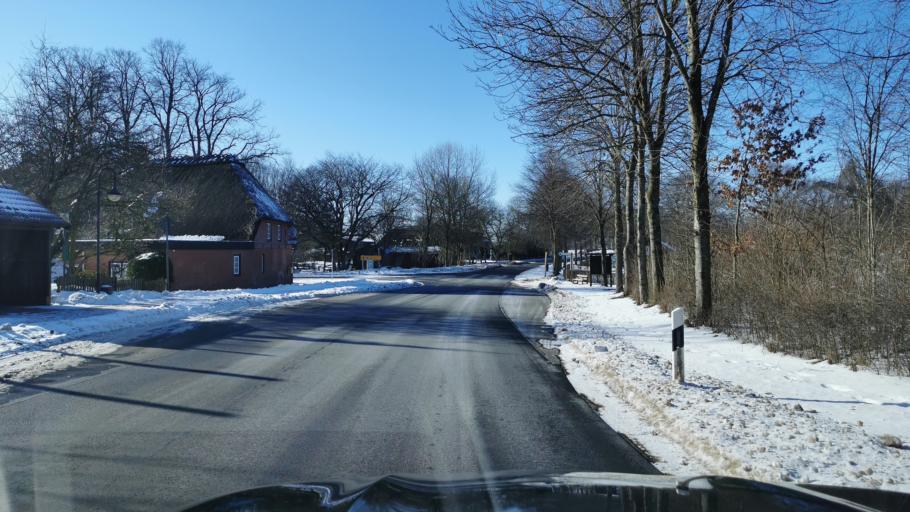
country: DE
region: Schleswig-Holstein
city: Grundhof
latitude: 54.7626
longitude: 9.6362
